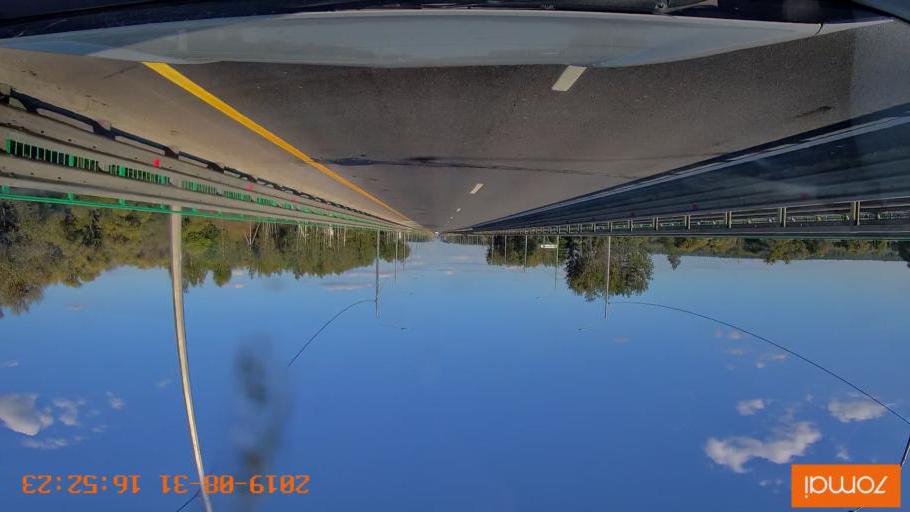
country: RU
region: Kaluga
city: Detchino
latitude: 54.7406
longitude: 36.1904
